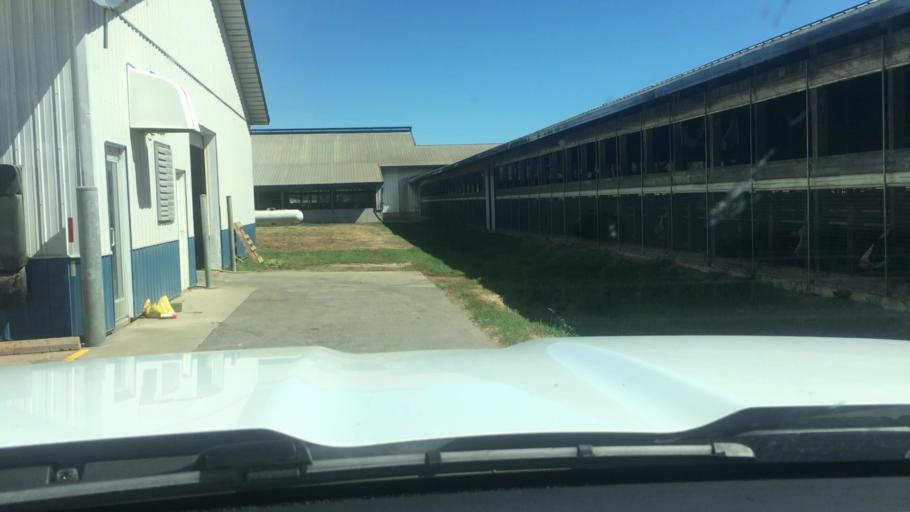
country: US
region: Michigan
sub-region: Montcalm County
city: Carson City
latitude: 43.2505
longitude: -84.7559
